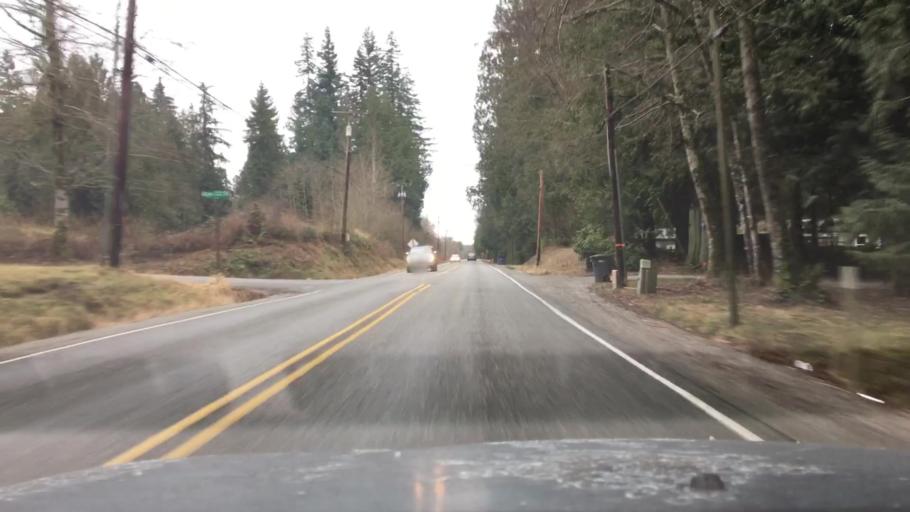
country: US
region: Washington
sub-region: Whatcom County
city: Sudden Valley
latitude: 48.6343
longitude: -122.3125
